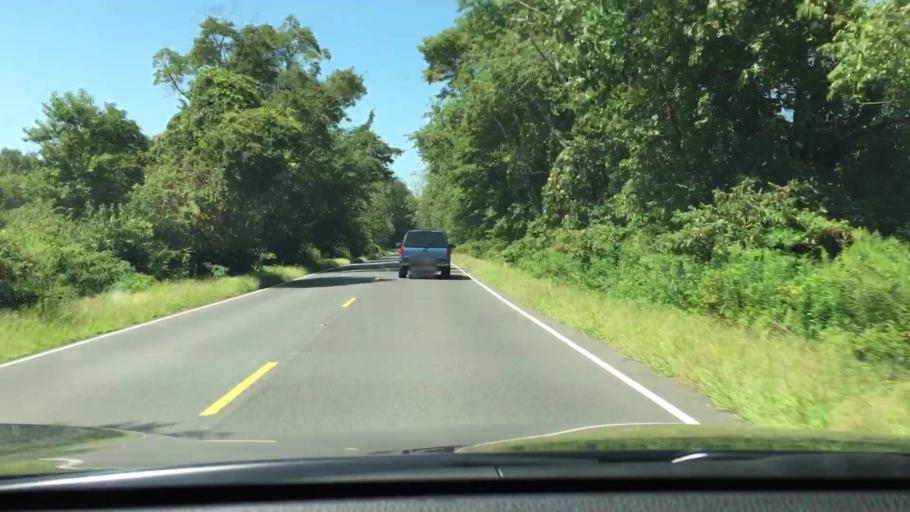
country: US
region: New Jersey
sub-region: Cape May County
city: Woodbine
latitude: 39.2609
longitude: -74.8986
